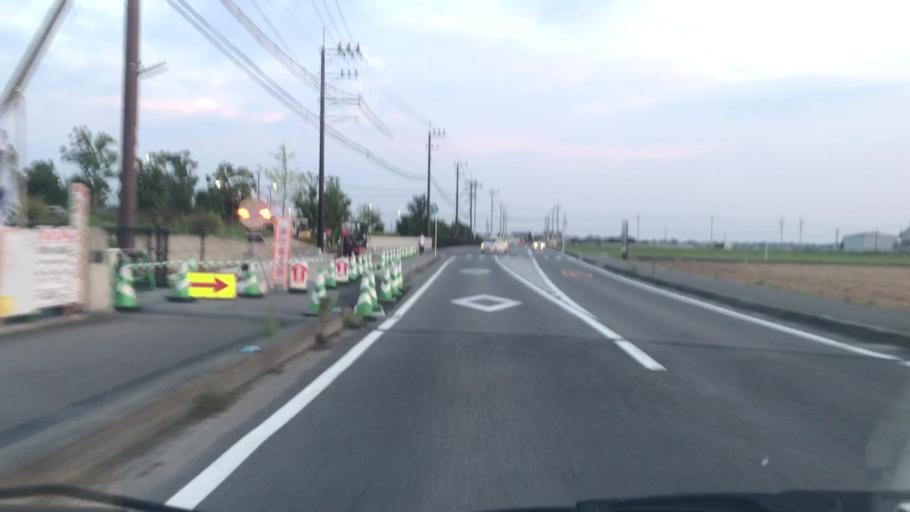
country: JP
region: Saga Prefecture
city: Saga-shi
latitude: 33.2424
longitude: 130.2664
